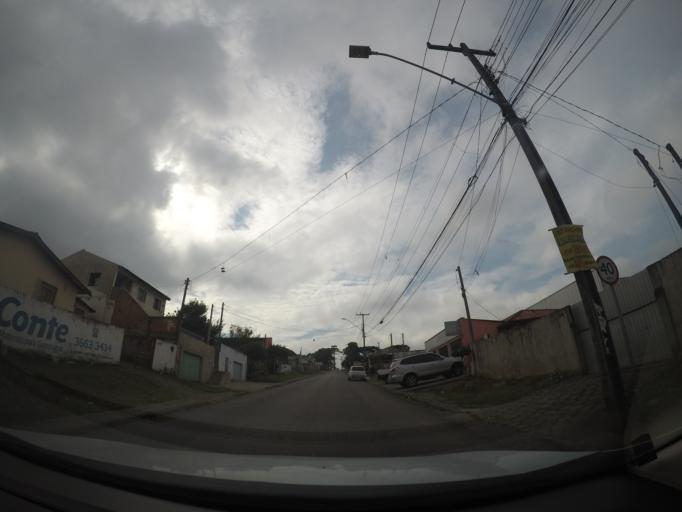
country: BR
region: Parana
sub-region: Colombo
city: Colombo
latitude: -25.3549
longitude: -49.2030
